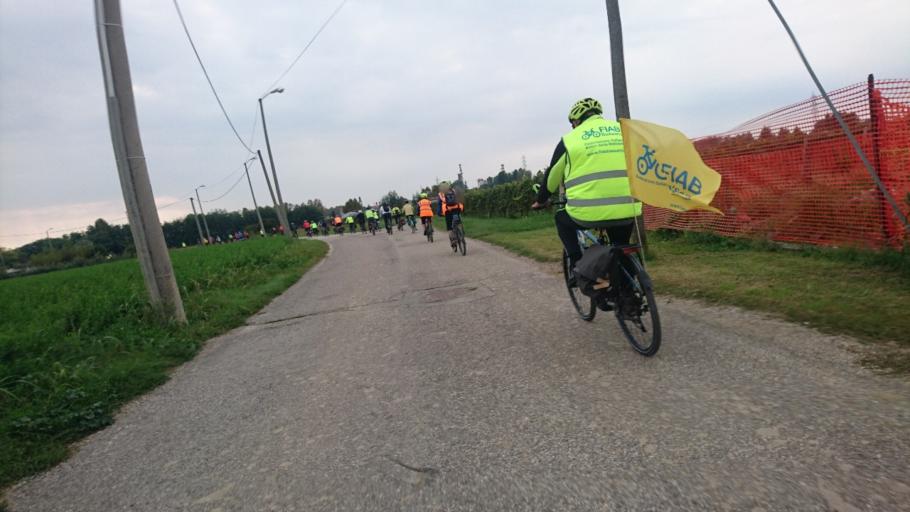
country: IT
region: Veneto
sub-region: Provincia di Verona
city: San Giovanni Lupatoto
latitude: 45.4075
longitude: 11.0591
